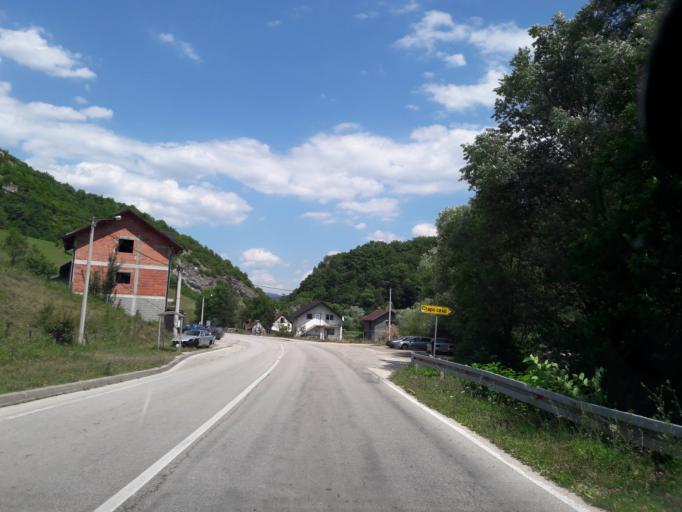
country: BA
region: Republika Srpska
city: Mrkonjic Grad
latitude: 44.4223
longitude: 17.1198
